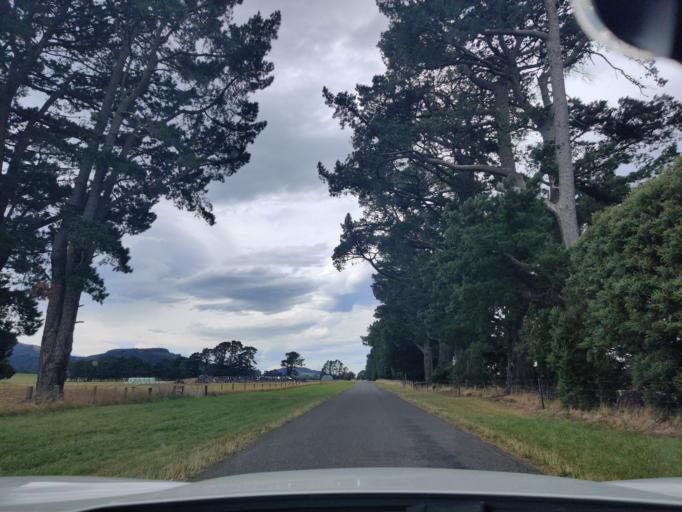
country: NZ
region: Wellington
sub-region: Masterton District
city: Masterton
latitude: -41.0245
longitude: 175.4569
